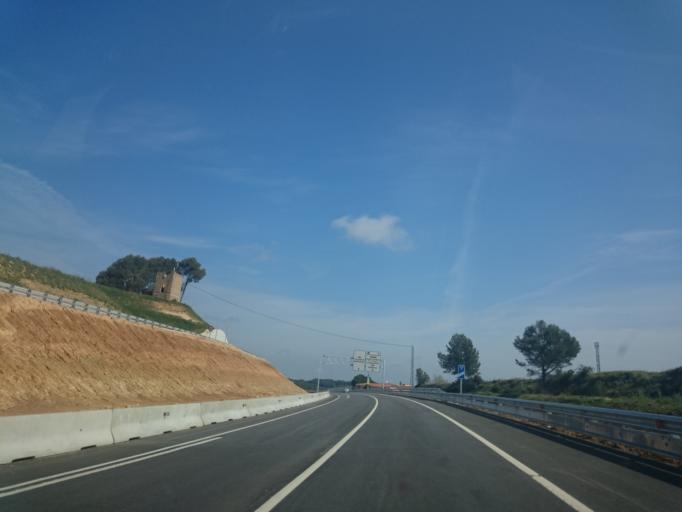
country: ES
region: Catalonia
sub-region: Provincia de Girona
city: Cervia de Ter
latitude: 42.0927
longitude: 2.8925
